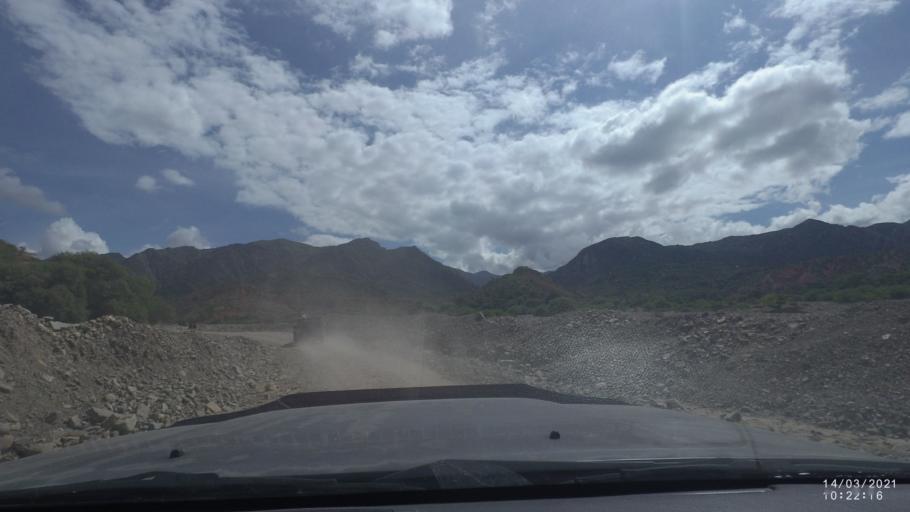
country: BO
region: Cochabamba
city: Cliza
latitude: -17.9216
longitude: -65.8720
